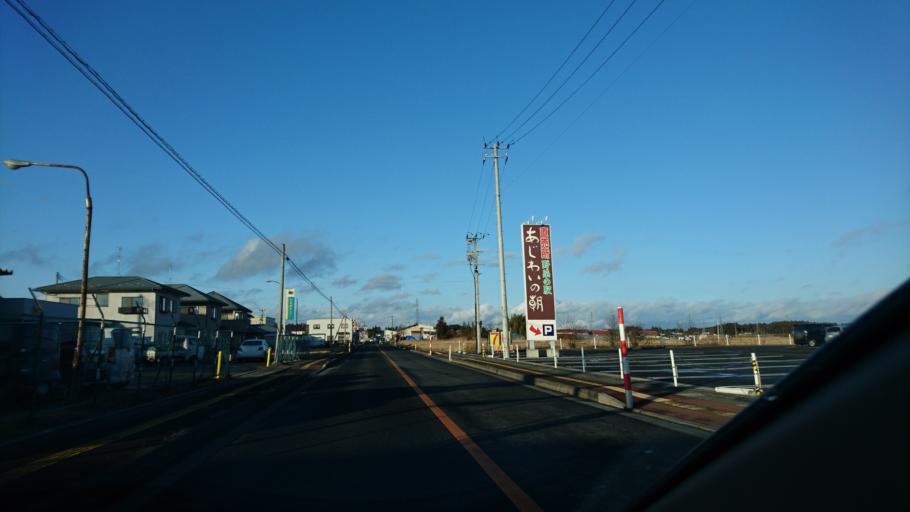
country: JP
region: Miyagi
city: Furukawa
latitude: 38.5778
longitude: 140.8602
